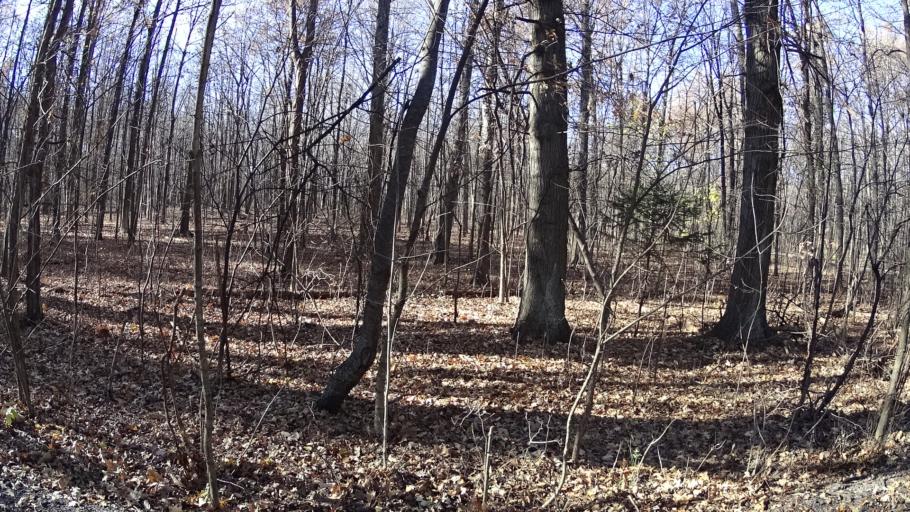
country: US
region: Ohio
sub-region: Lorain County
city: Avon Center
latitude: 41.4478
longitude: -82.0138
